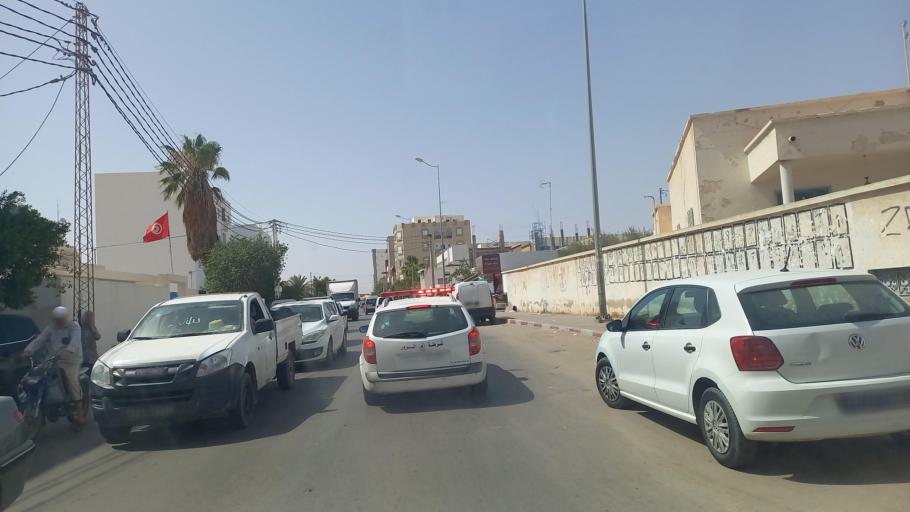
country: TN
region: Madanin
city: Medenine
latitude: 33.3416
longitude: 10.4883
